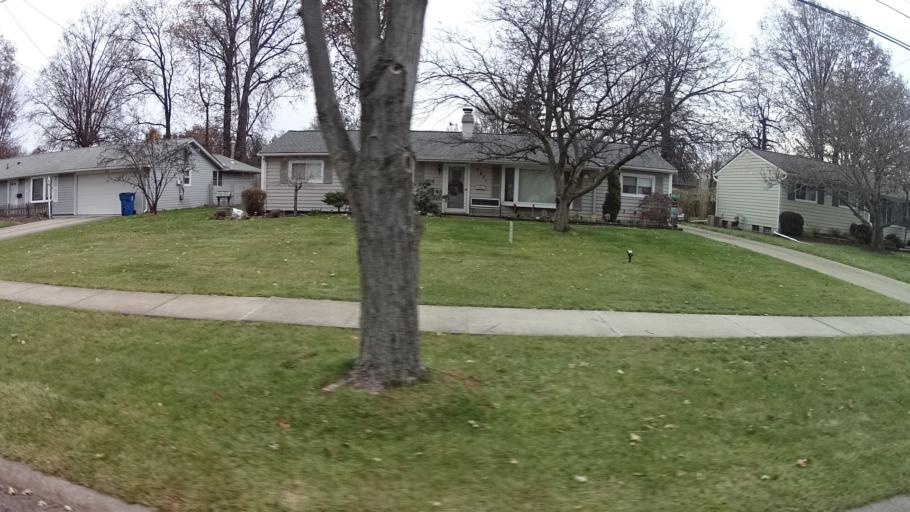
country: US
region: Ohio
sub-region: Lorain County
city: North Ridgeville
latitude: 41.4037
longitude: -82.0026
